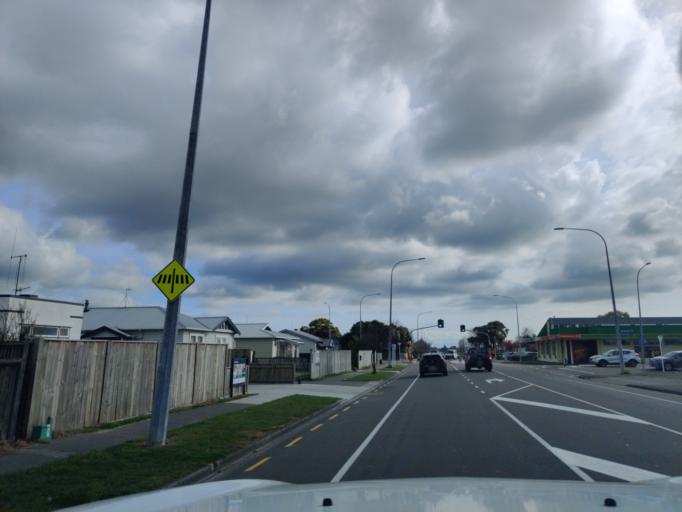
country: NZ
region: Manawatu-Wanganui
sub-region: Palmerston North City
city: Palmerston North
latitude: -40.3323
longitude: 175.6157
